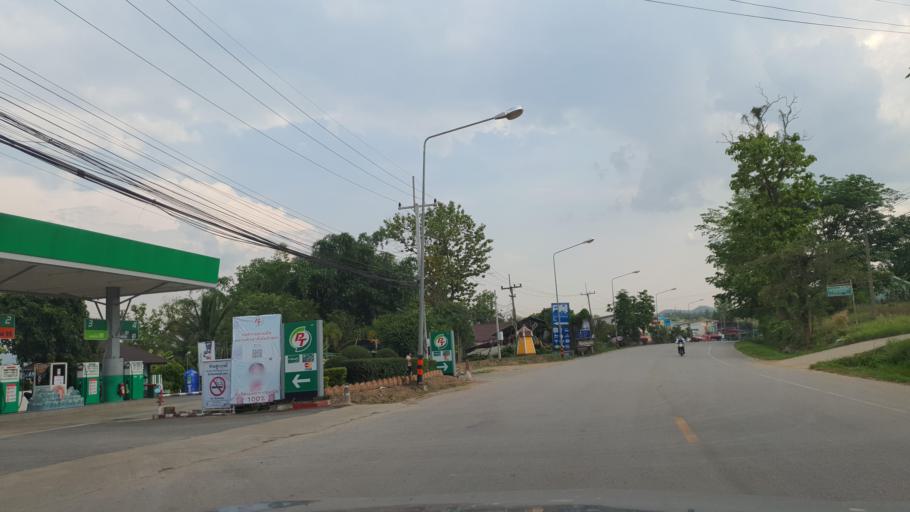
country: TH
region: Chiang Mai
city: Pai
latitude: 19.3494
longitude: 98.4351
